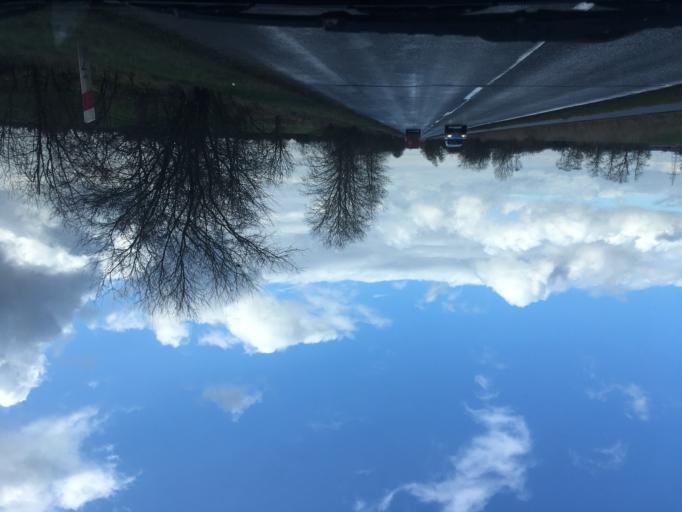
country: PL
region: Pomeranian Voivodeship
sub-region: Powiat gdanski
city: Cedry Wielkie
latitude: 54.3285
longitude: 18.7633
